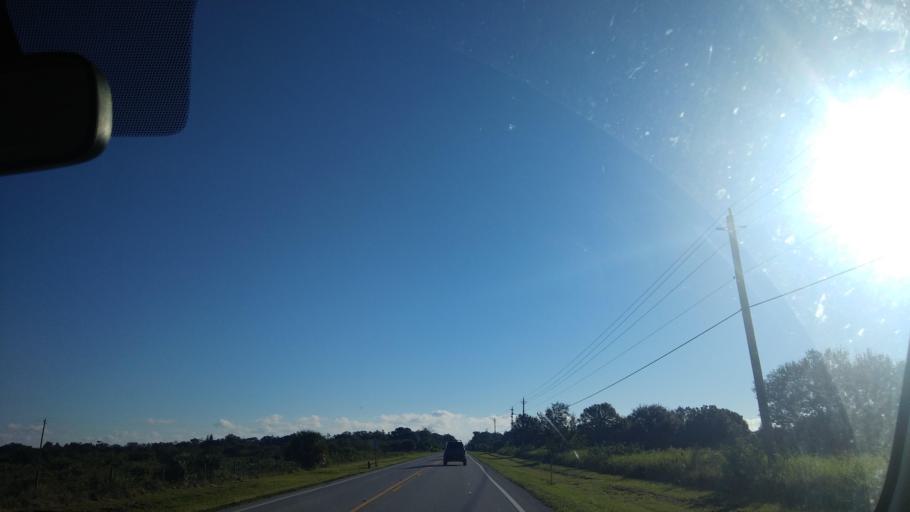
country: US
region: Florida
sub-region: Indian River County
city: Sebastian
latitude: 27.7489
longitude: -80.4924
